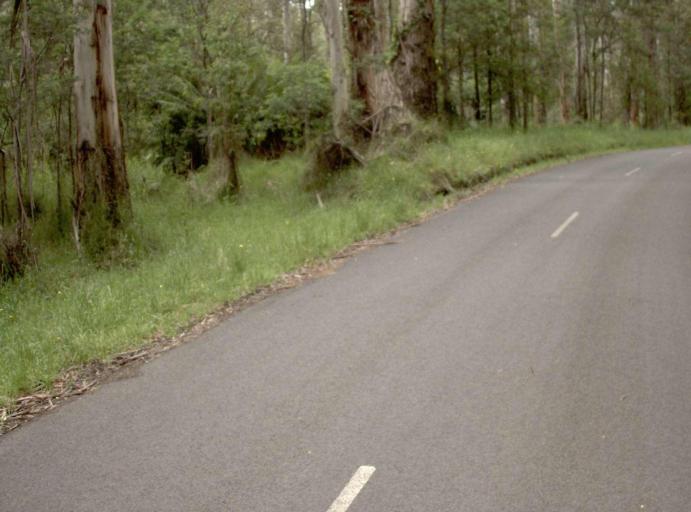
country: AU
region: Victoria
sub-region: Baw Baw
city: Warragul
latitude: -37.9155
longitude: 146.1061
